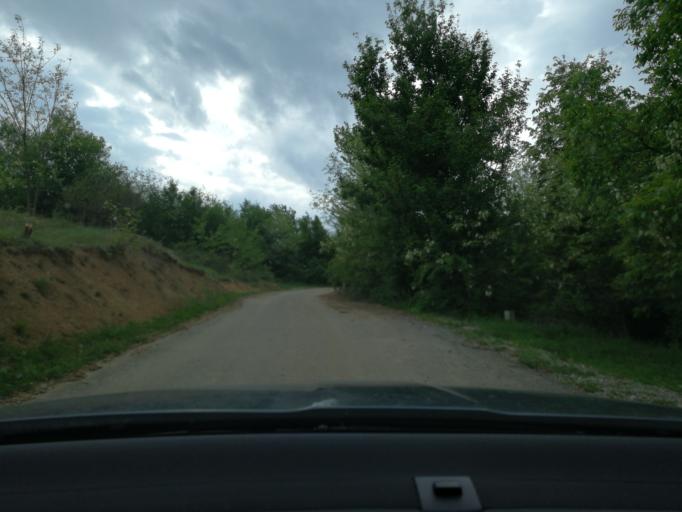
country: RO
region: Prahova
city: Cornu de Sus
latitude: 45.1743
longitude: 25.7048
